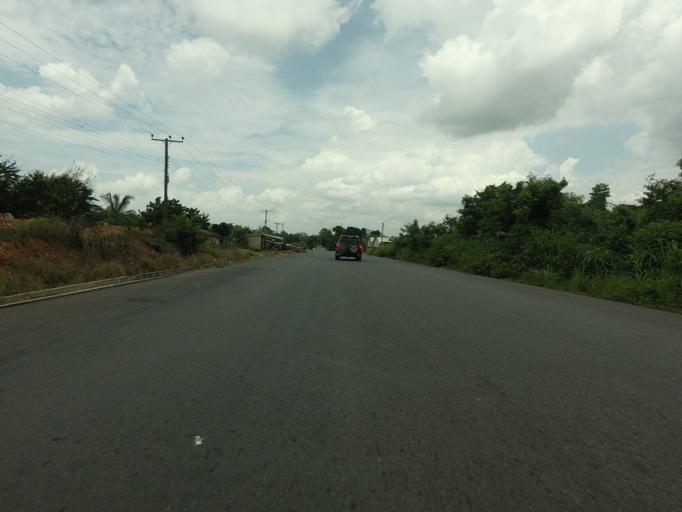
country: GH
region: Volta
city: Ho
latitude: 6.4178
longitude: 0.1722
